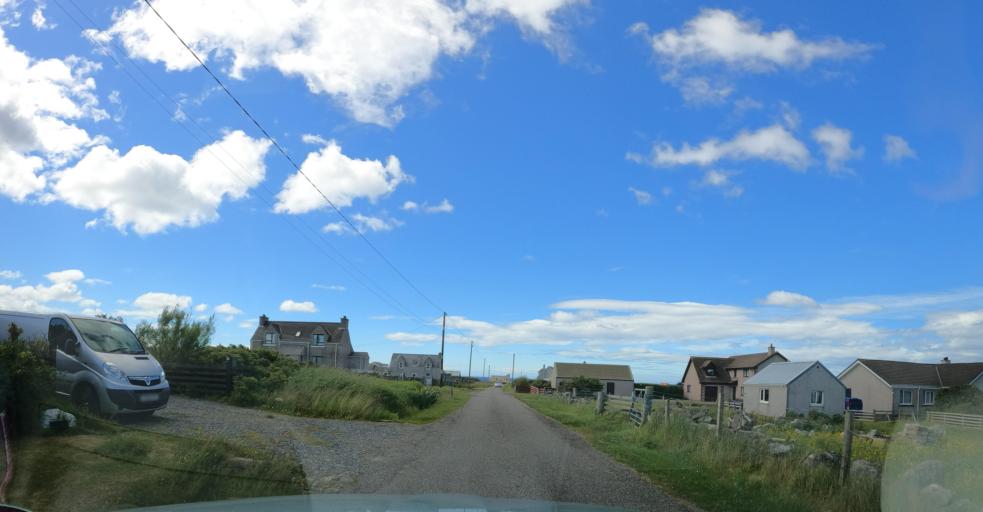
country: GB
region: Scotland
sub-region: Eilean Siar
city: Isle of Lewis
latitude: 58.3582
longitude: -6.5587
